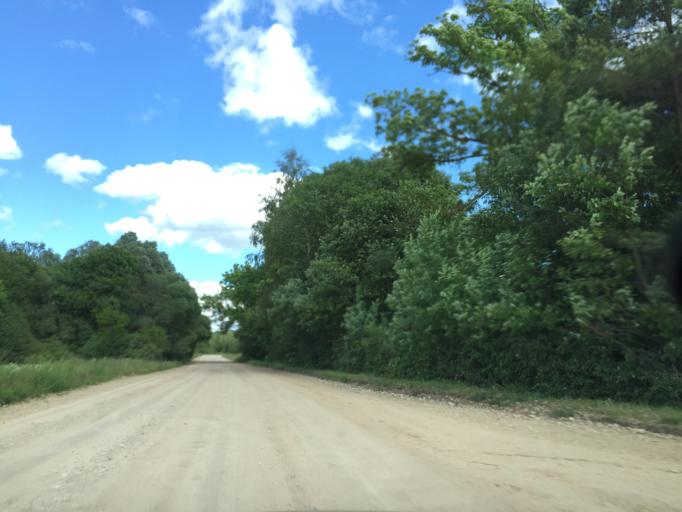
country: LV
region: Vecumnieki
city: Vecumnieki
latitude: 56.4022
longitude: 24.5418
